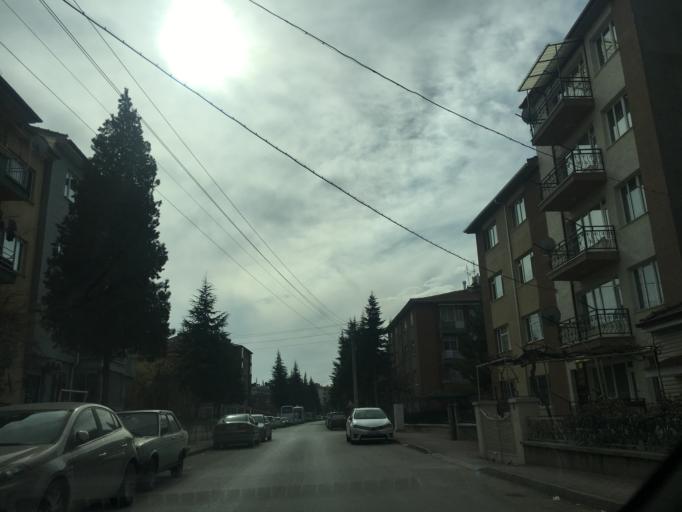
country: TR
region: Eskisehir
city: Eskisehir
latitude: 39.7724
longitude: 30.5045
